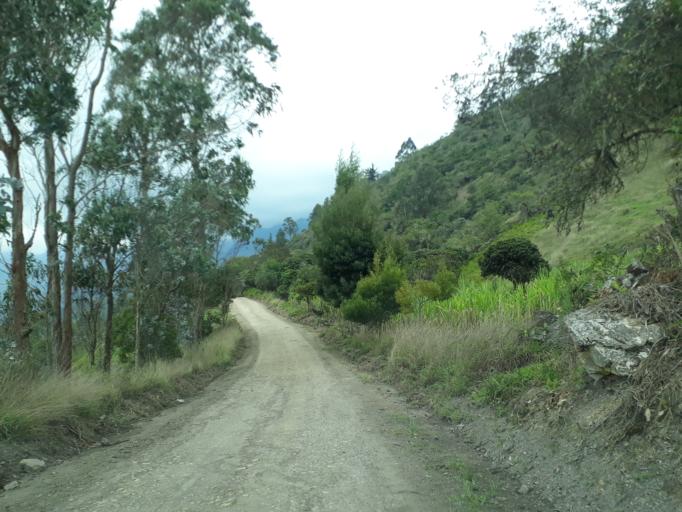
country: CO
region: Cundinamarca
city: Manta
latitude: 5.0225
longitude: -73.5408
